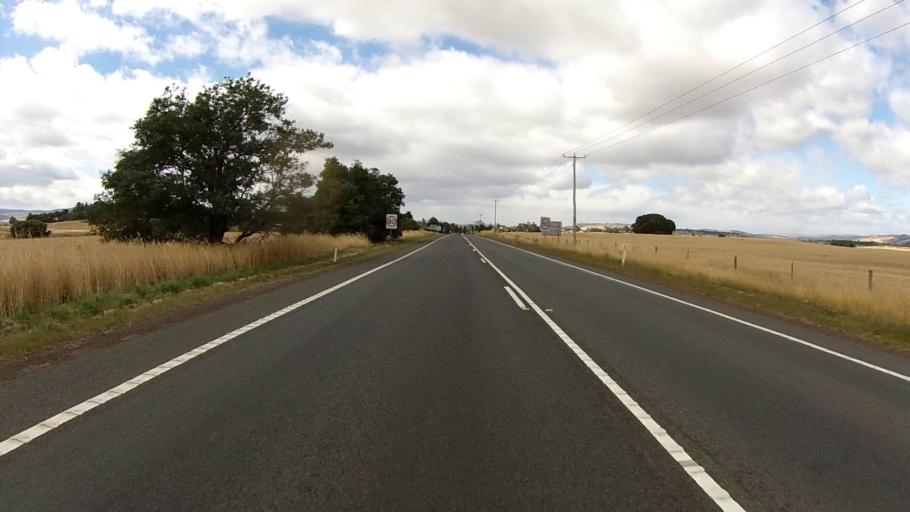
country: AU
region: Tasmania
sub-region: Northern Midlands
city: Evandale
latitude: -41.9112
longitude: 147.4818
